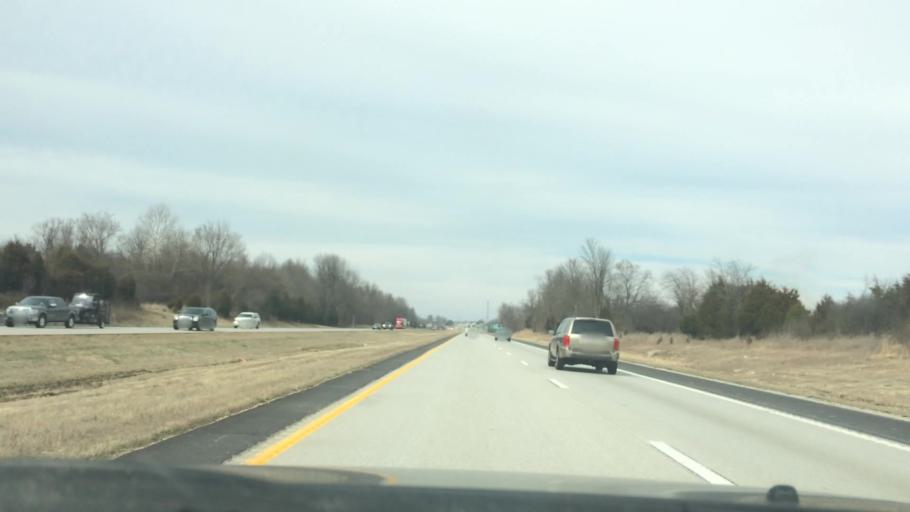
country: US
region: Missouri
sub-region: Polk County
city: Bolivar
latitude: 37.4663
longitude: -93.3543
